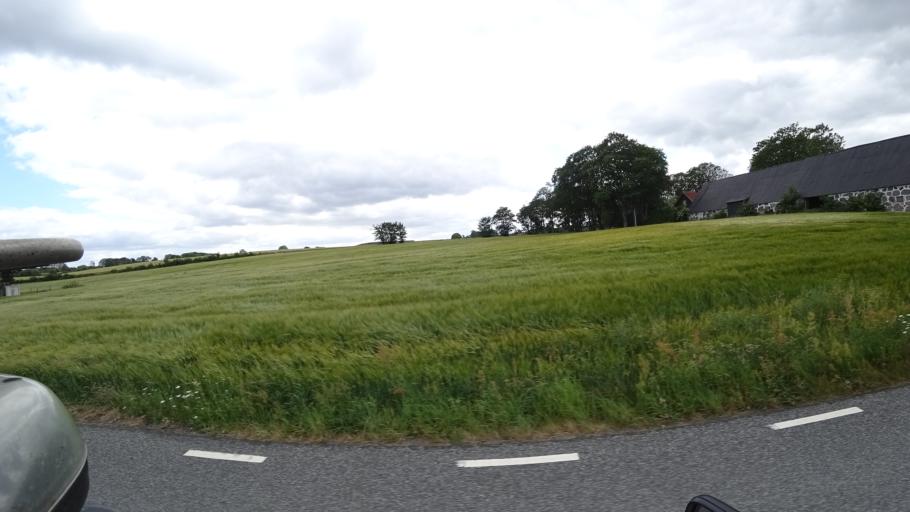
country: SE
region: Skane
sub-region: Kristianstads Kommun
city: Degeberga
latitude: 55.6984
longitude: 14.0316
